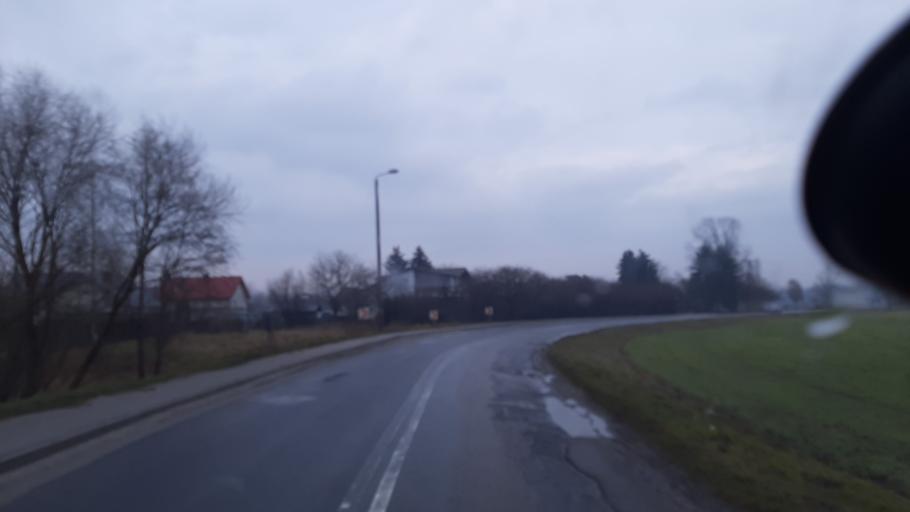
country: PL
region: Lublin Voivodeship
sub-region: Powiat lubartowski
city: Serniki
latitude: 51.4329
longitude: 22.6429
